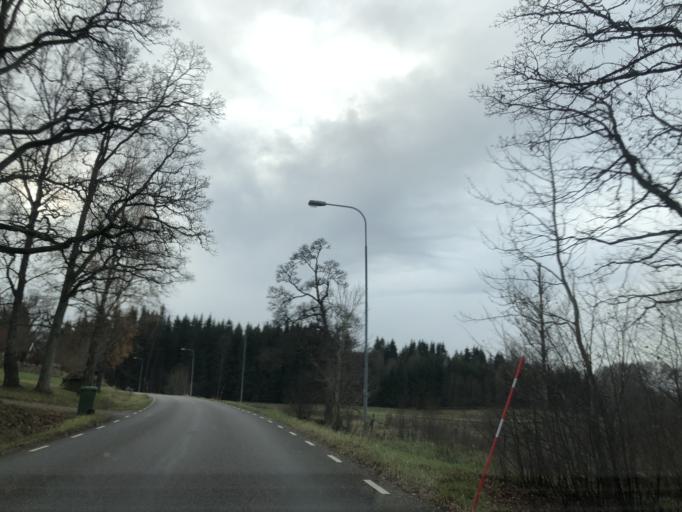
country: SE
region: Vaestra Goetaland
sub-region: Ulricehamns Kommun
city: Ulricehamn
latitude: 57.6799
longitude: 13.4110
